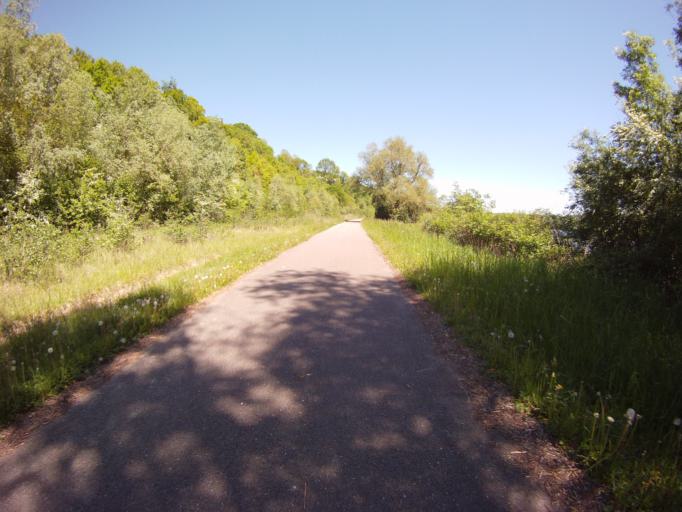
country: FR
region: Lorraine
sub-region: Departement de Meurthe-et-Moselle
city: Villey-Saint-Etienne
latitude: 48.7348
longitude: 5.9840
